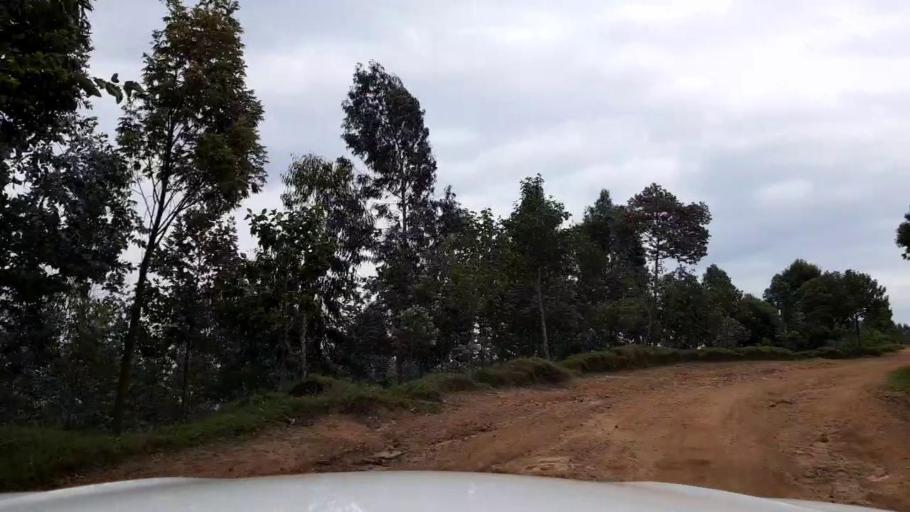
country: RW
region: Western Province
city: Kibuye
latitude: -1.9593
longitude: 29.4035
